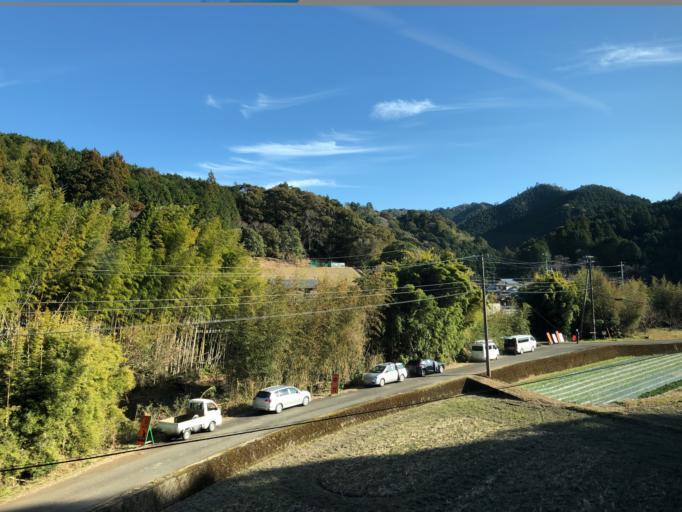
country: JP
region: Kochi
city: Nakamura
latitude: 33.1233
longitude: 133.1193
